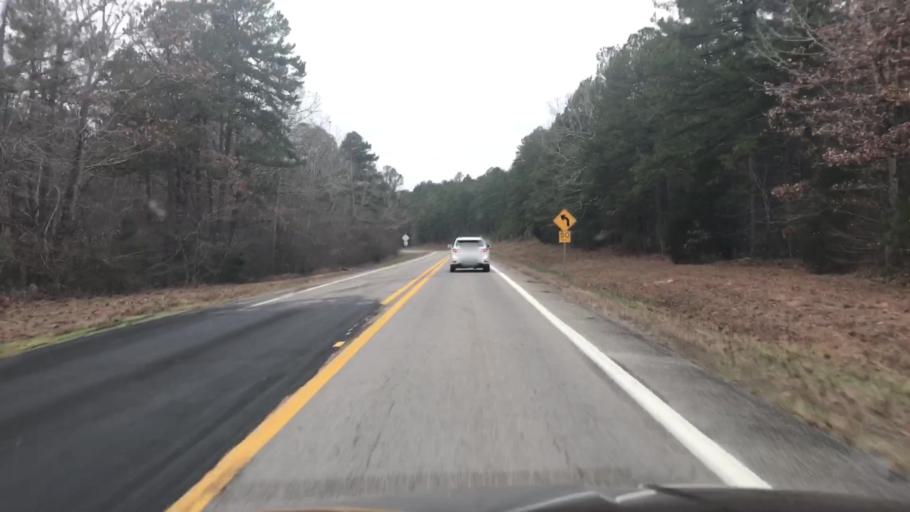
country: US
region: Arkansas
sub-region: Montgomery County
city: Mount Ida
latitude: 34.6862
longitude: -93.8740
